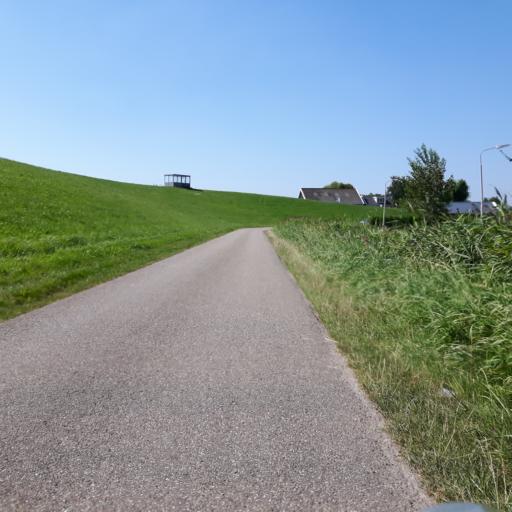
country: NL
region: Zeeland
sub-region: Gemeente Reimerswaal
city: Yerseke
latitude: 51.4135
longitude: 4.0683
